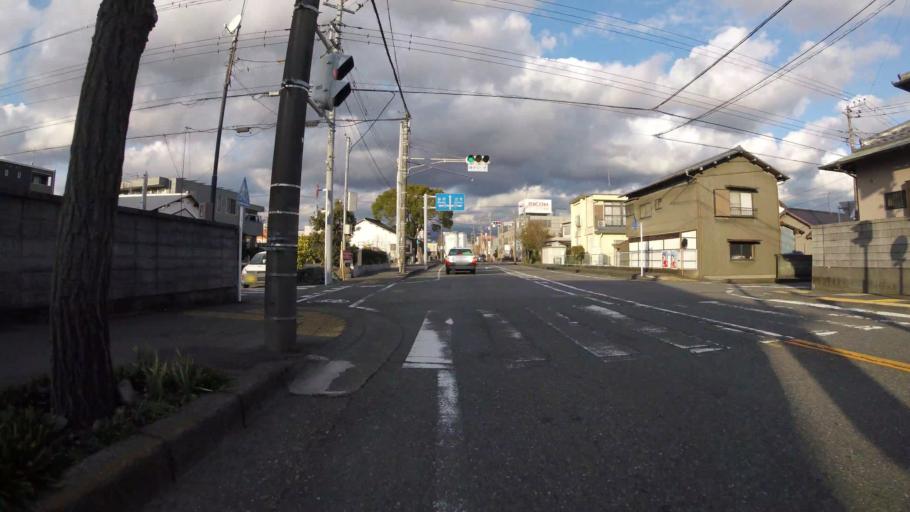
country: JP
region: Shizuoka
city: Fuji
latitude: 35.1555
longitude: 138.6838
